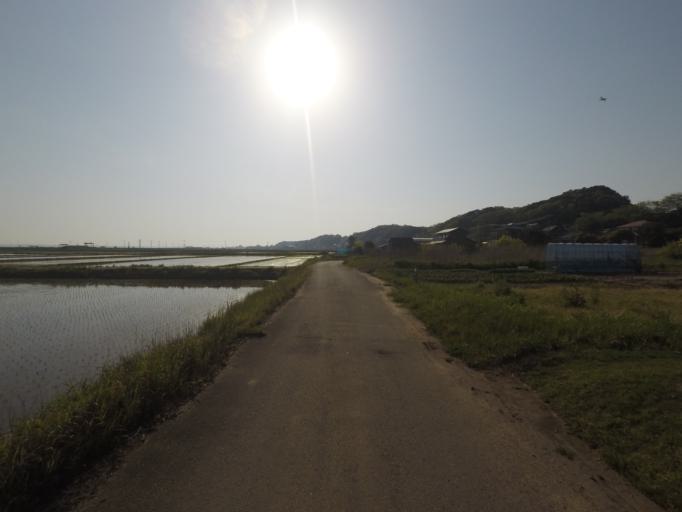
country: JP
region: Ibaraki
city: Inashiki
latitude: 36.0649
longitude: 140.3511
